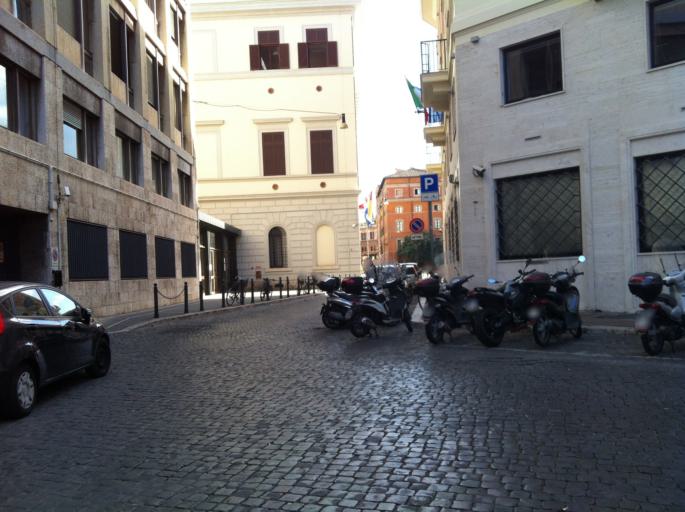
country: VA
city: Vatican City
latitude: 41.8878
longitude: 12.4744
